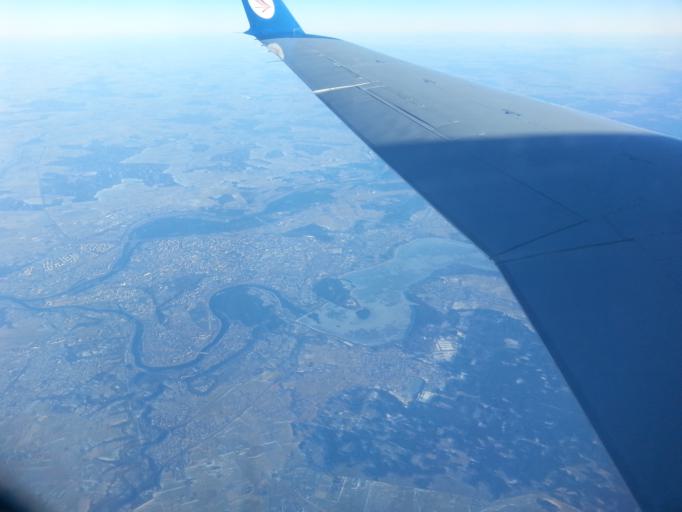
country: LT
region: Kauno apskritis
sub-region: Kauno rajonas
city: Garliava
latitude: 54.7510
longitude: 23.9629
